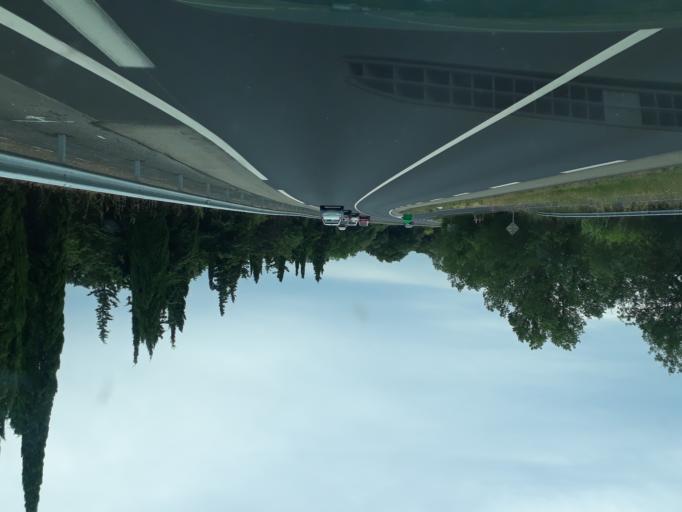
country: FR
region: Languedoc-Roussillon
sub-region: Departement de l'Herault
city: Saint-Thibery
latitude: 43.3927
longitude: 3.4128
